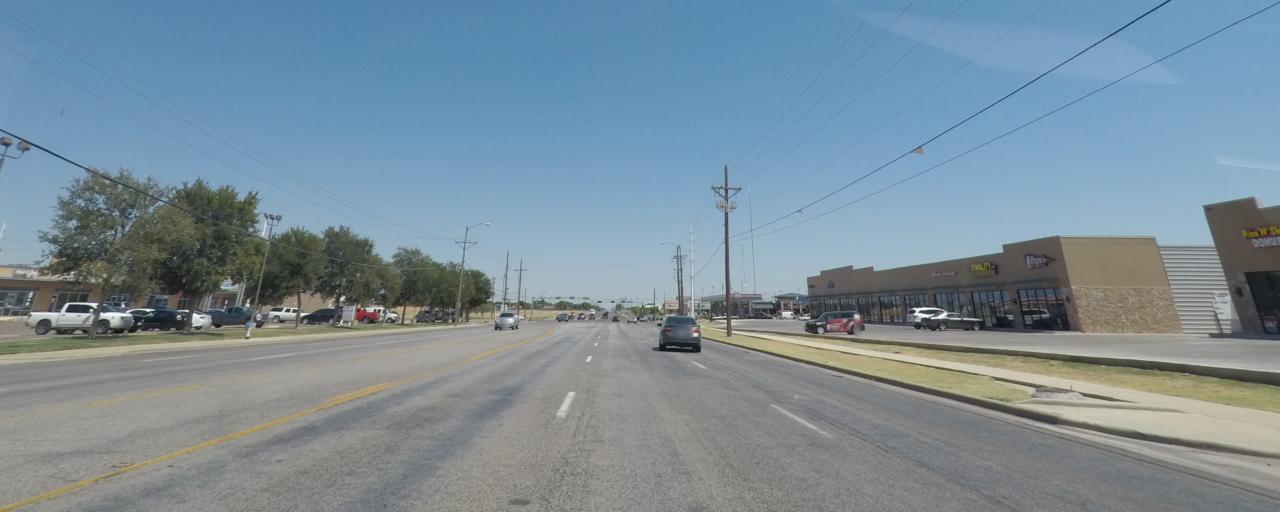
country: US
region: Texas
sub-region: Lubbock County
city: Lubbock
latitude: 33.5052
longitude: -101.8900
